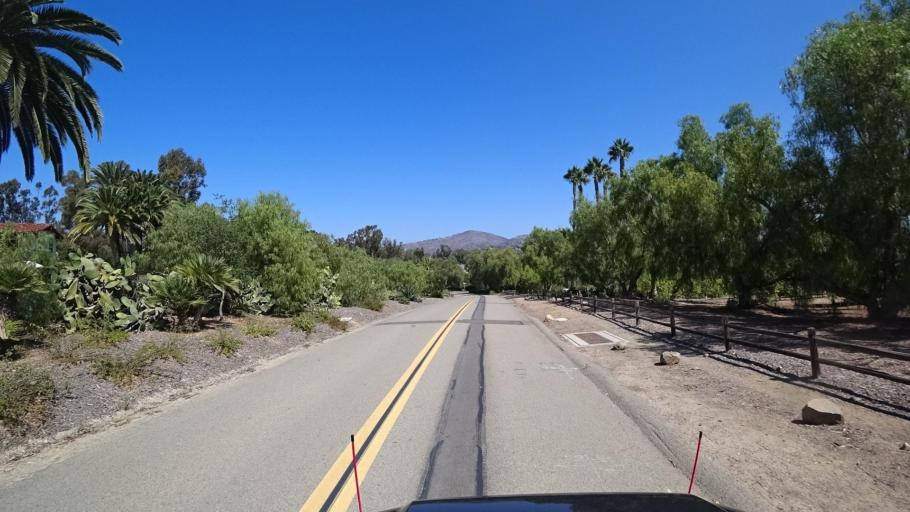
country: US
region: California
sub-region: San Diego County
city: Rancho Santa Fe
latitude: 33.0234
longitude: -117.1818
